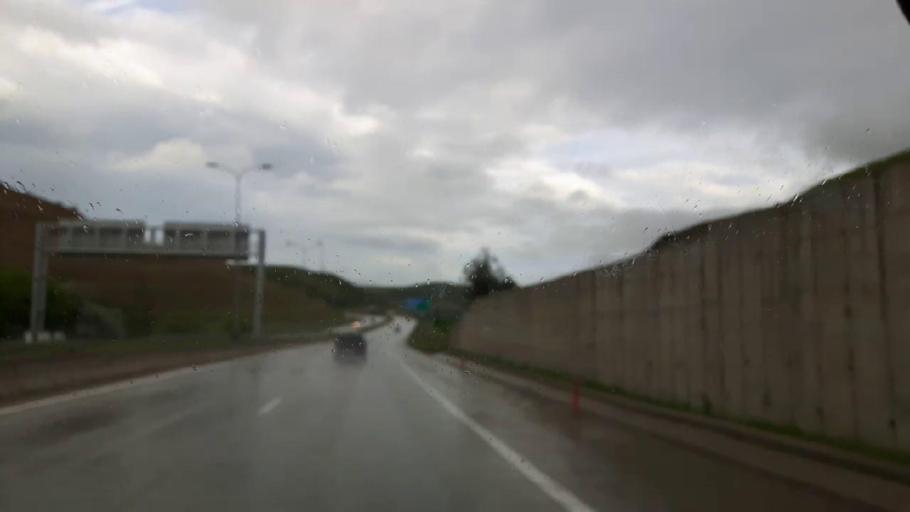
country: GE
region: Shida Kartli
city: Kaspi
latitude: 41.9985
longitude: 44.3967
